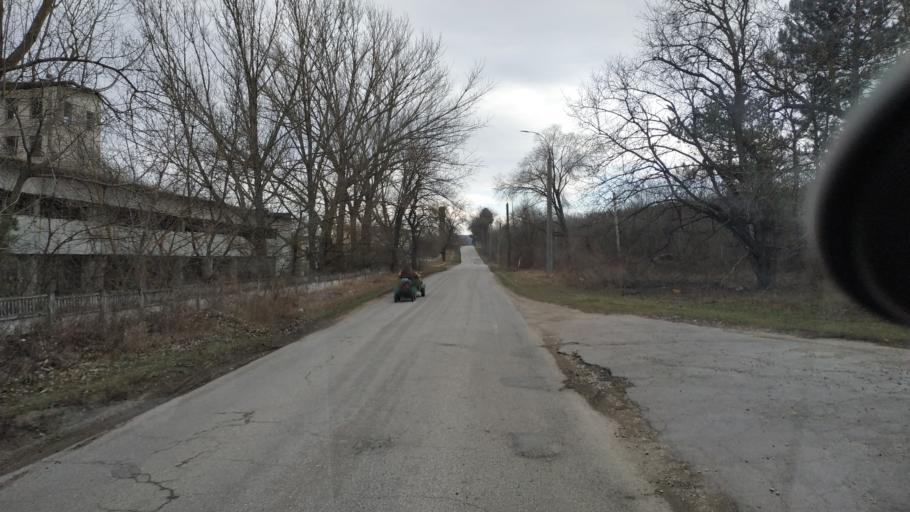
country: MD
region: Chisinau
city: Vadul lui Voda
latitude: 47.1013
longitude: 29.0676
